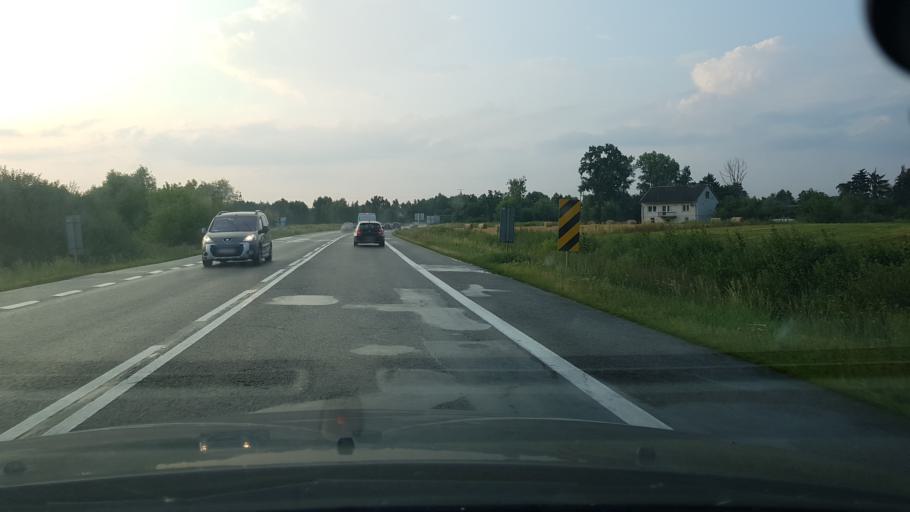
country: PL
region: Masovian Voivodeship
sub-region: Powiat ciechanowski
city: Glinojeck
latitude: 52.7987
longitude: 20.2701
